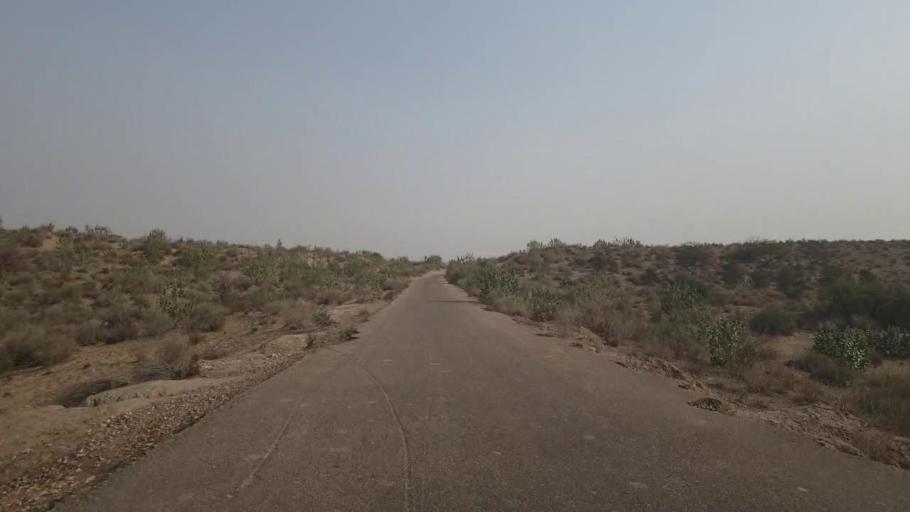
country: PK
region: Sindh
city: Chor
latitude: 25.4491
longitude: 69.9633
